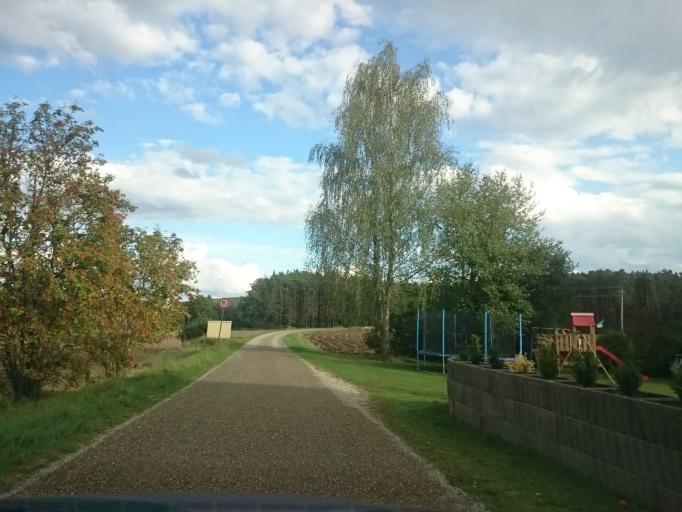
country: DE
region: Bavaria
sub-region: Regierungsbezirk Mittelfranken
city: Hilpoltstein
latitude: 49.1556
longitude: 11.1740
